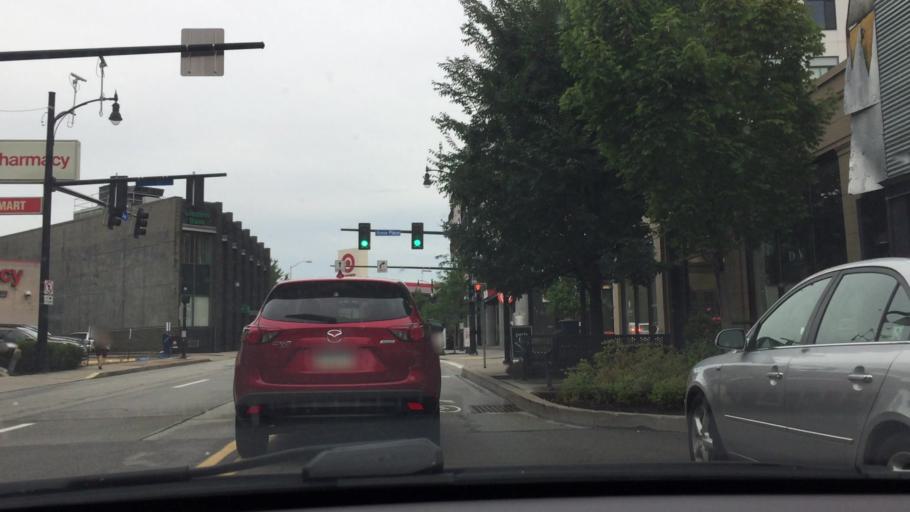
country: US
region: Pennsylvania
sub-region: Allegheny County
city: Bloomfield
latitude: 40.4601
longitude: -79.9244
